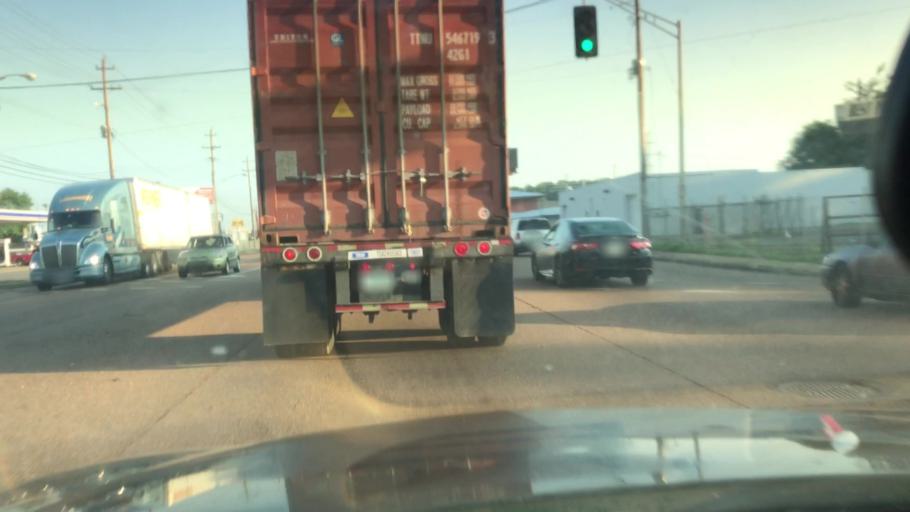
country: US
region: Mississippi
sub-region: De Soto County
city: Southaven
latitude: 35.0730
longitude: -89.9475
